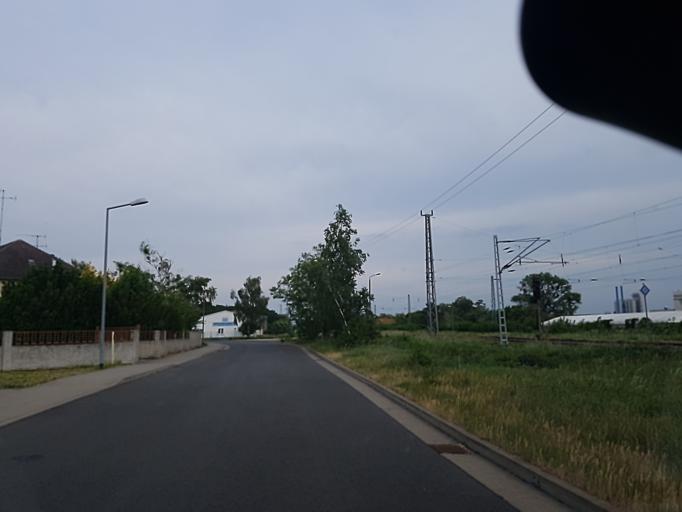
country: DE
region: Saxony-Anhalt
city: Jessen
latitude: 51.7962
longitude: 12.9489
